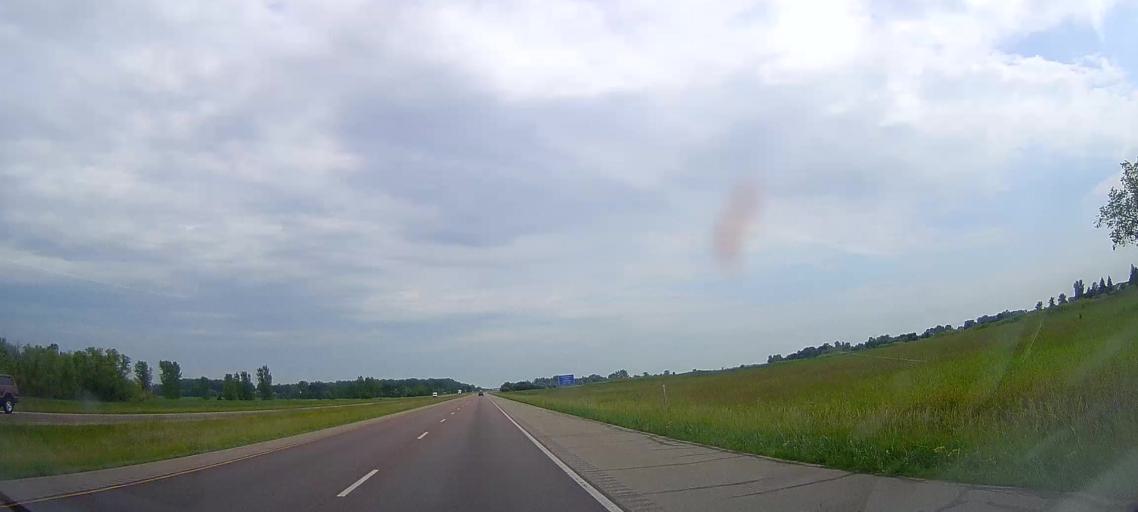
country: US
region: Nebraska
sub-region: Thurston County
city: Macy
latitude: 42.1433
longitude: -96.2143
